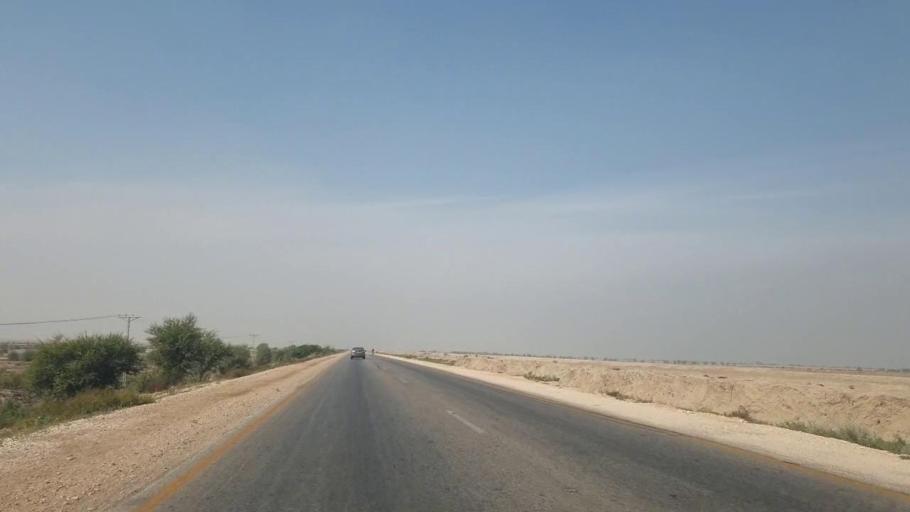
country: PK
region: Sindh
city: Sann
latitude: 25.9060
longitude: 68.2286
